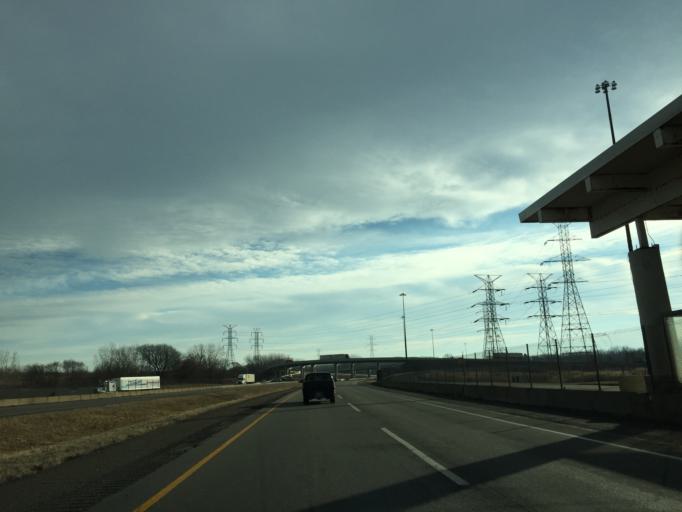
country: US
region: Indiana
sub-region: Lake County
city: Lake Station
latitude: 41.5930
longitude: -87.2379
